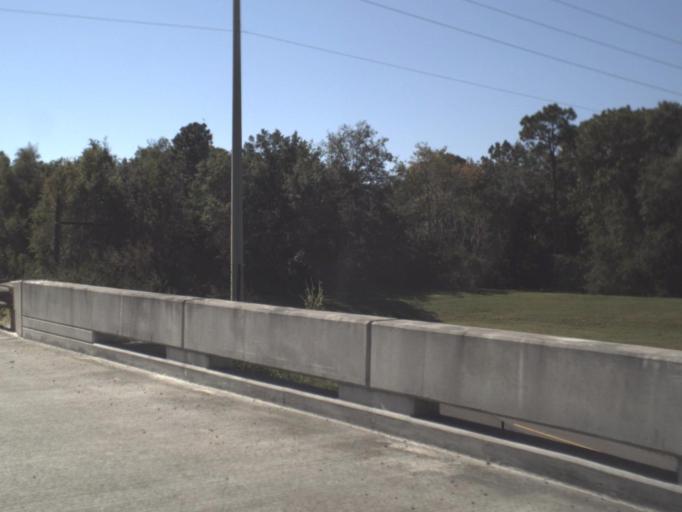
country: US
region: Florida
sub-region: Hernando County
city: Brookridge
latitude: 28.6143
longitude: -82.4936
